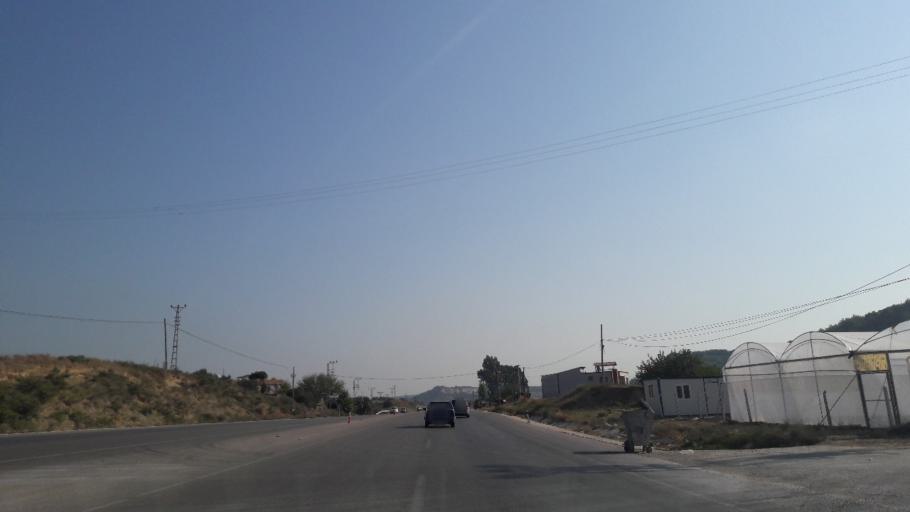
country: TR
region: Adana
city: Yuregir
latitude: 37.0660
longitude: 35.4492
